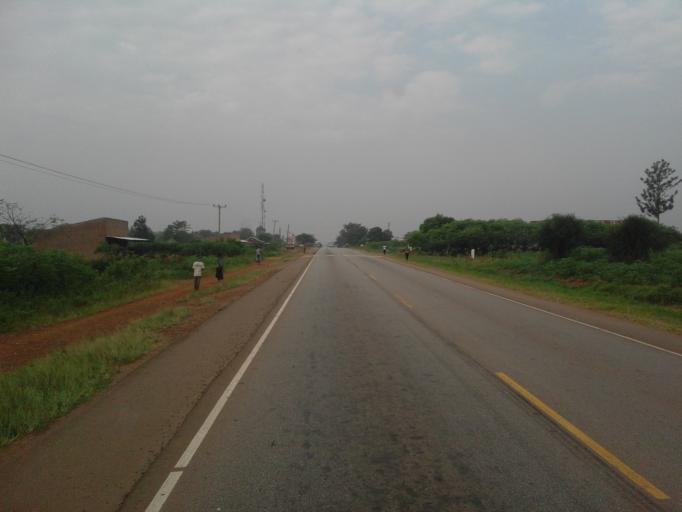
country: UG
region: Eastern Region
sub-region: Tororo District
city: Tororo
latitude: 0.6267
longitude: 34.1006
